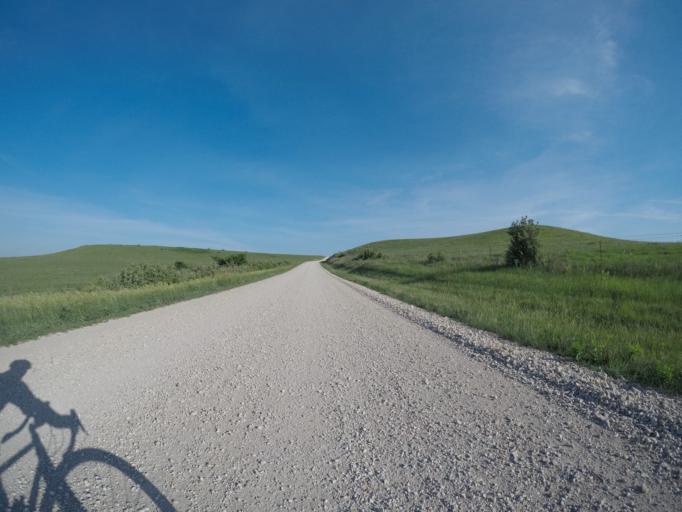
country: US
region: Kansas
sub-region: Riley County
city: Manhattan
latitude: 39.0419
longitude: -96.4922
